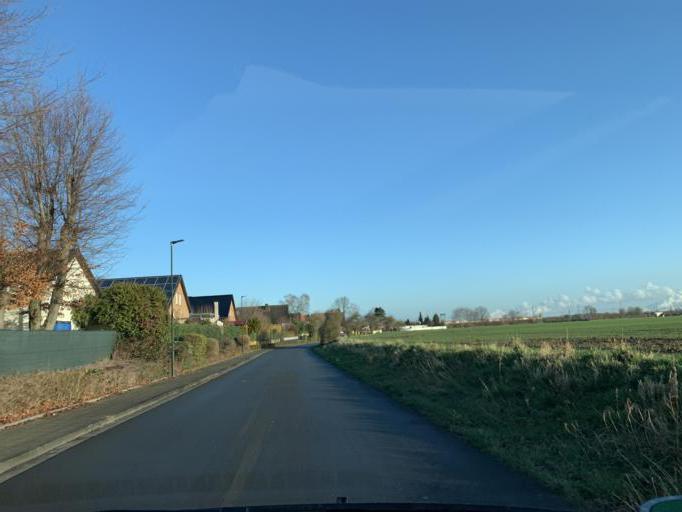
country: DE
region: North Rhine-Westphalia
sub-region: Regierungsbezirk Koln
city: Merzenich
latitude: 50.8626
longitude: 6.5865
